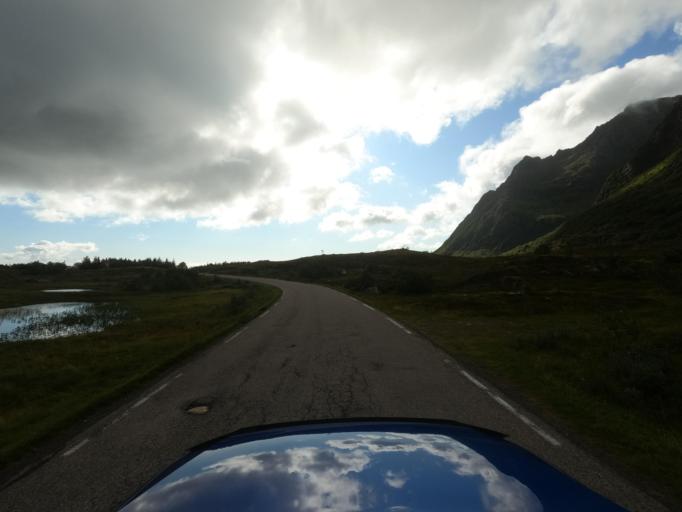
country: NO
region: Nordland
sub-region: Vestvagoy
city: Evjen
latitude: 68.1864
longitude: 13.8585
